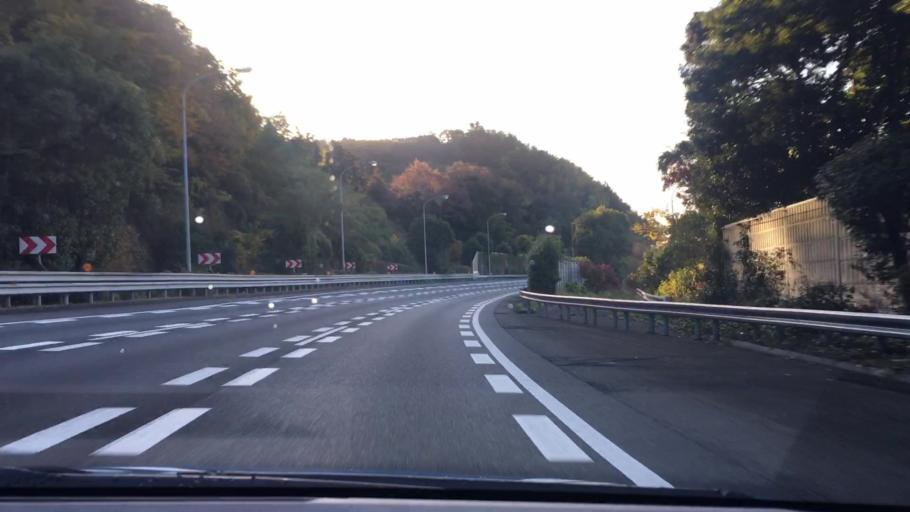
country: JP
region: Kanagawa
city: Hadano
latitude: 35.3664
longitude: 139.1012
